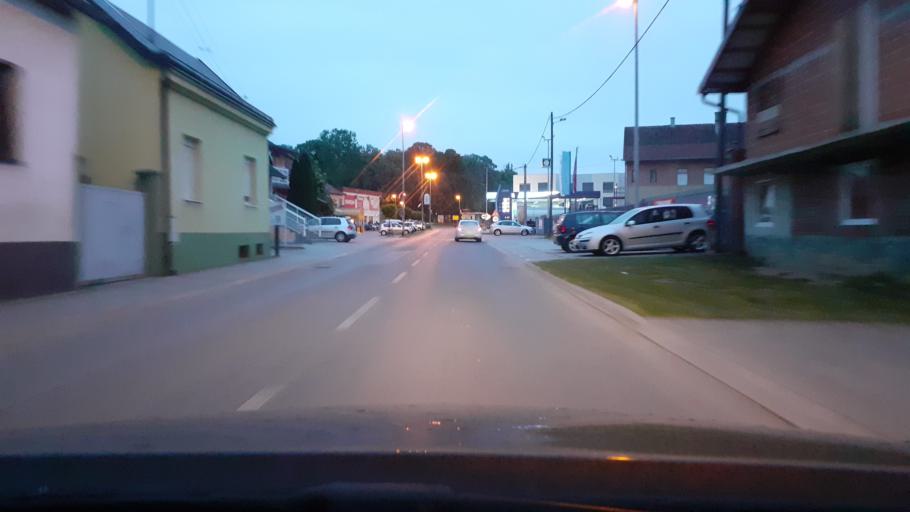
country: HR
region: Pozesko-Slavonska
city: Pleternica
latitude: 45.2850
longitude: 17.8039
